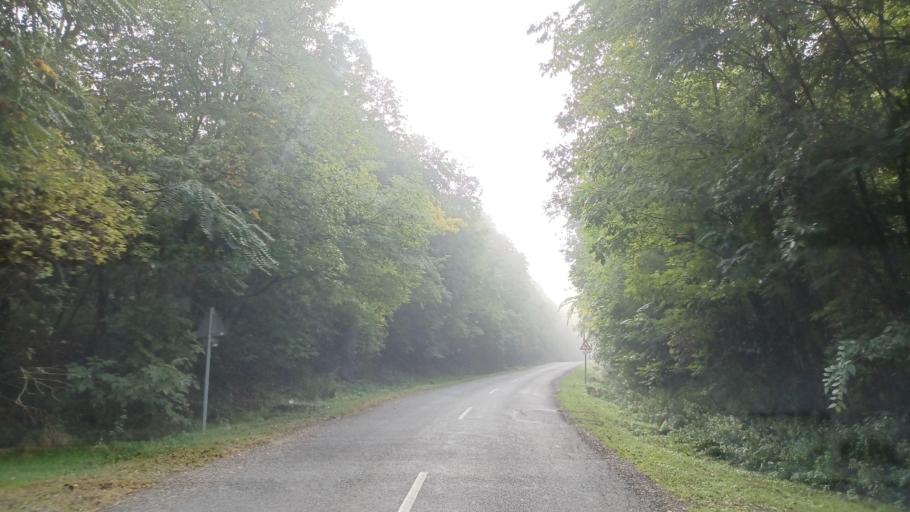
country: HU
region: Tolna
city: Pincehely
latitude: 46.6799
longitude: 18.4654
